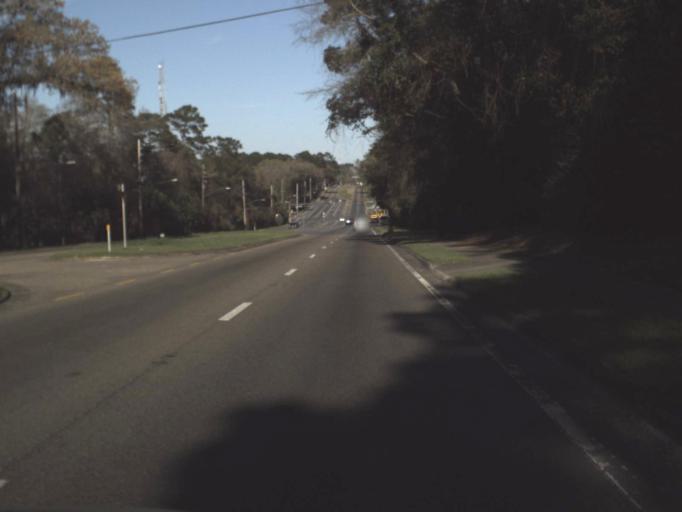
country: US
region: Florida
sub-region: Leon County
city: Tallahassee
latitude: 30.4512
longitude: -84.2522
